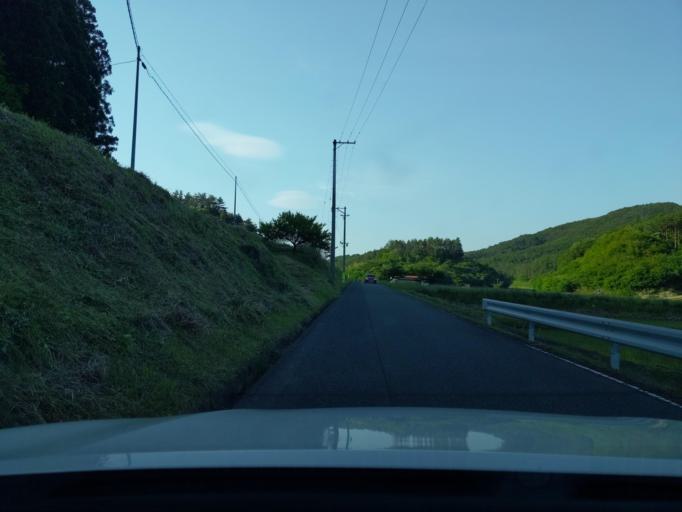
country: JP
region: Fukushima
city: Motomiya
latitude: 37.5166
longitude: 140.3301
